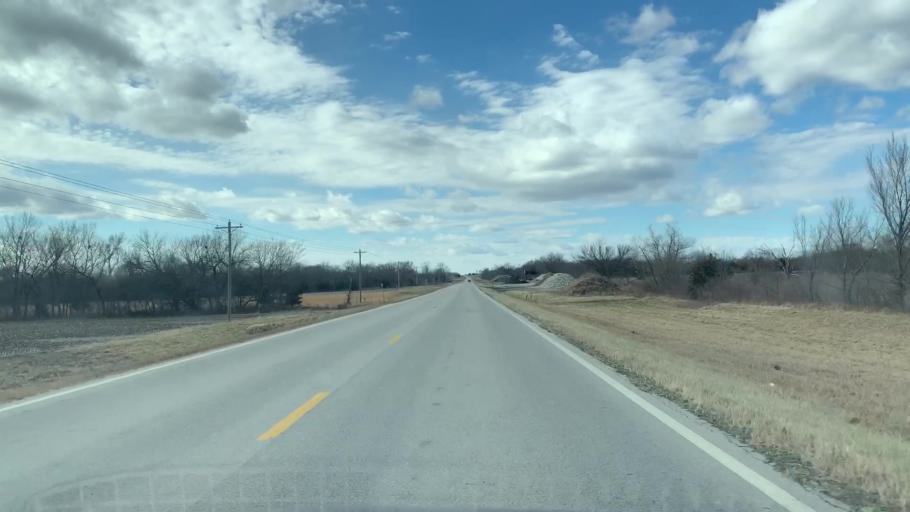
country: US
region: Kansas
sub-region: Neosho County
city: Erie
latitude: 37.5293
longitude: -95.2842
